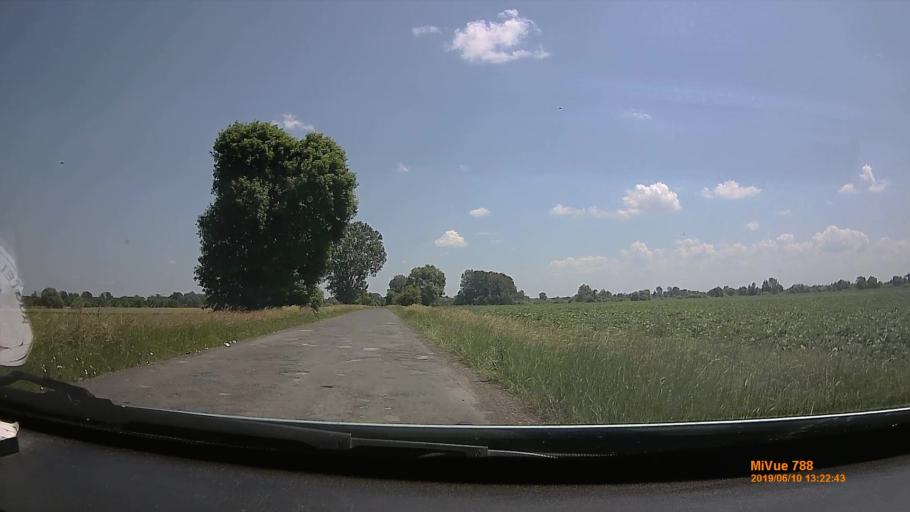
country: HU
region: Borsod-Abauj-Zemplen
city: Tiszaluc
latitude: 48.0289
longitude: 21.0858
